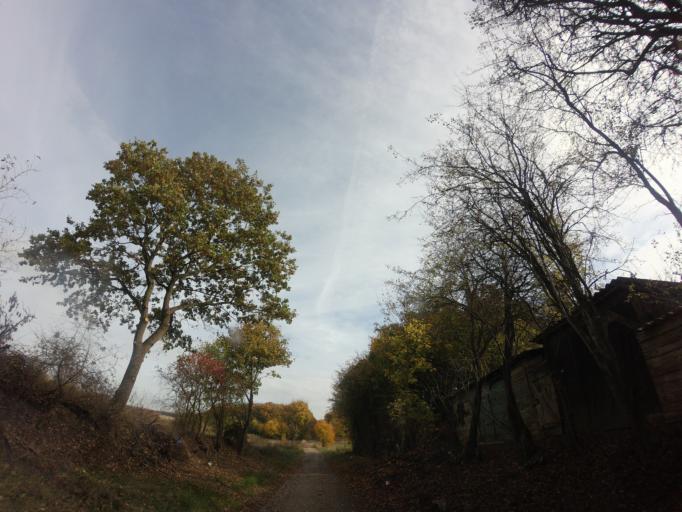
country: PL
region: West Pomeranian Voivodeship
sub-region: Powiat choszczenski
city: Recz
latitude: 53.2638
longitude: 15.6217
